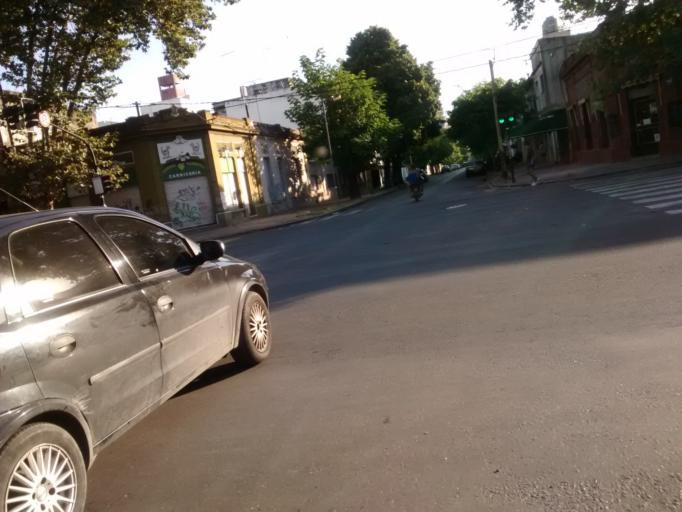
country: AR
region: Buenos Aires
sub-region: Partido de La Plata
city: La Plata
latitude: -34.9185
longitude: -57.9308
